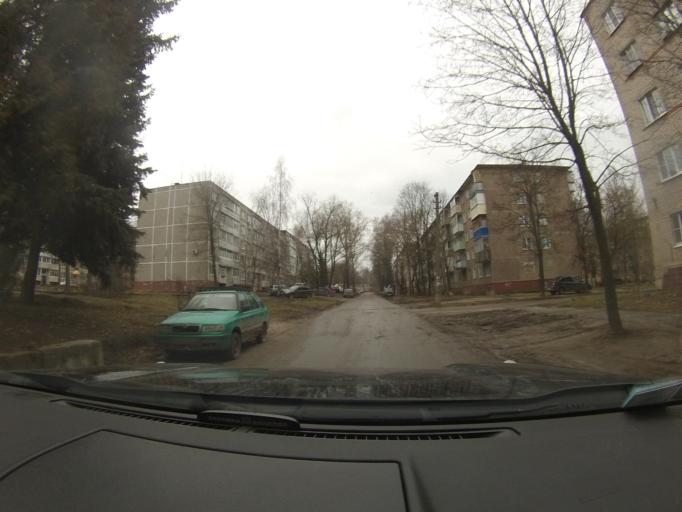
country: RU
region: Moskovskaya
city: Lopatinskiy
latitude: 55.3437
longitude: 38.7272
